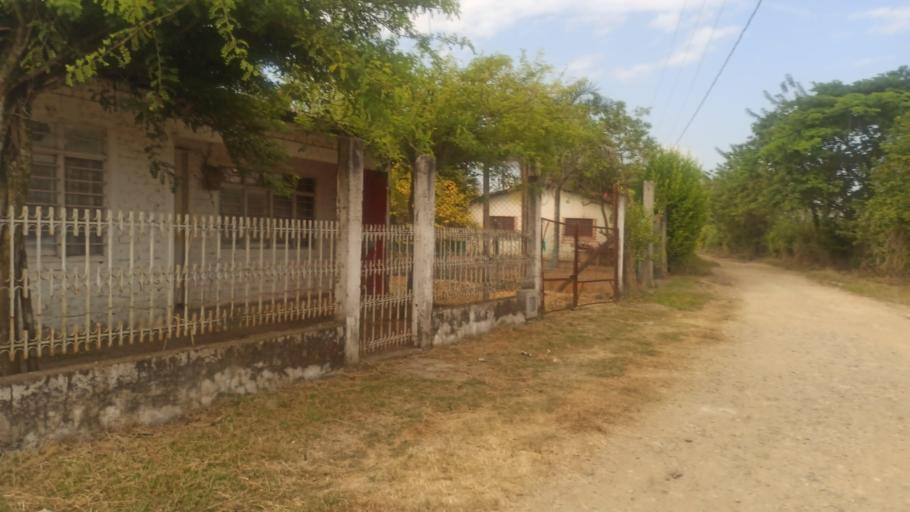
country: CO
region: Valle del Cauca
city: Jamundi
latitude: 3.1275
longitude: -76.5604
